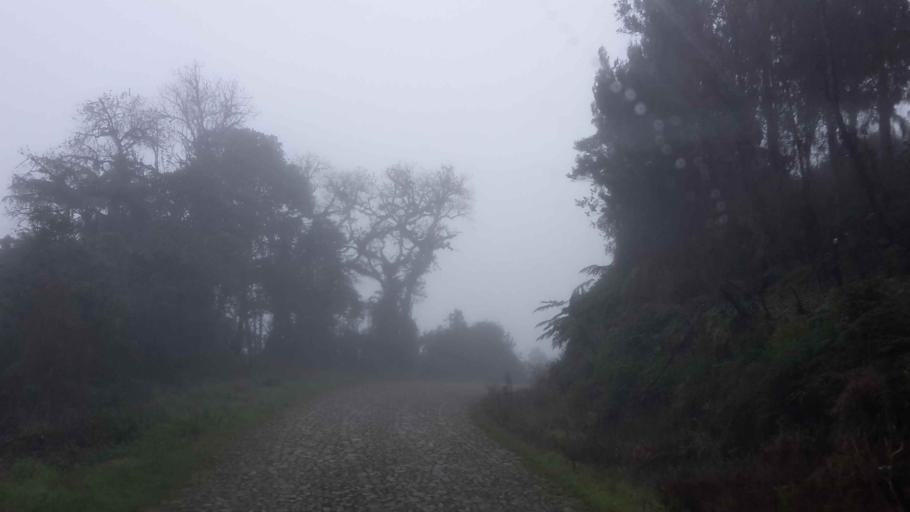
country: BO
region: Cochabamba
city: Colomi
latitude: -17.1209
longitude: -65.9628
